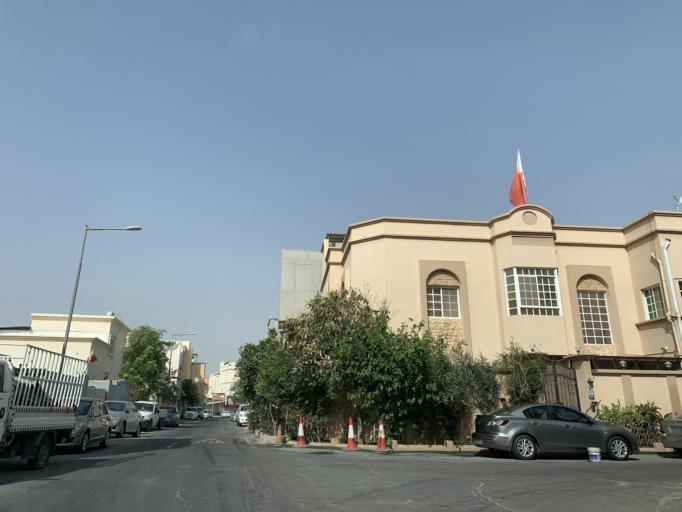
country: BH
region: Northern
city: Madinat `Isa
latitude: 26.1786
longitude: 50.5633
